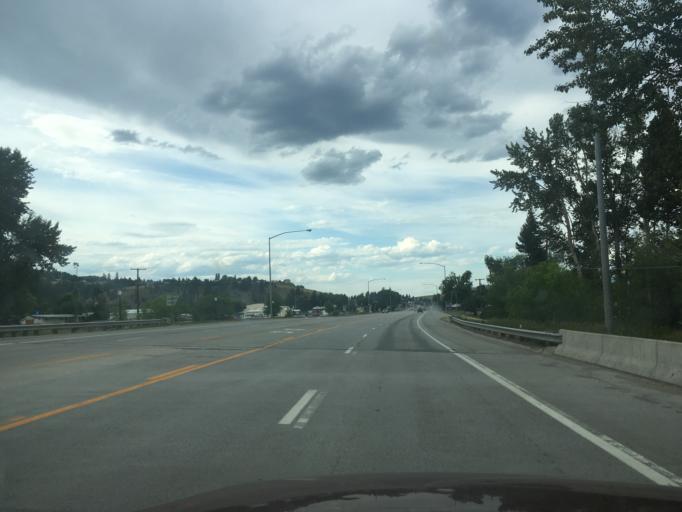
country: US
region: Montana
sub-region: Missoula County
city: Lolo
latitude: 46.7496
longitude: -114.0830
